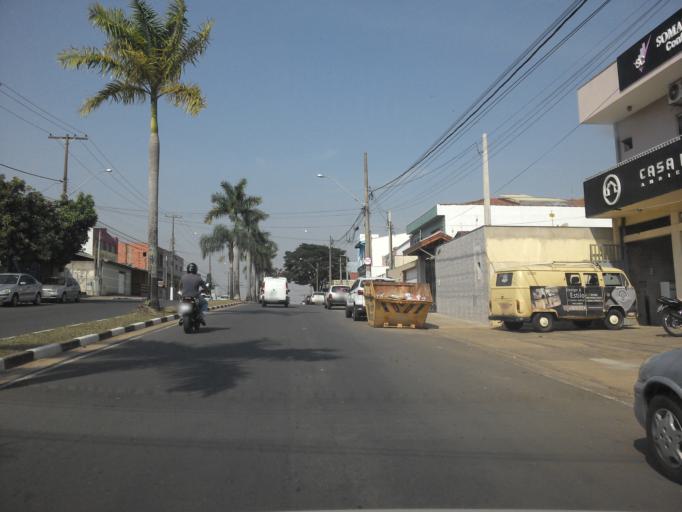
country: BR
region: Sao Paulo
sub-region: Hortolandia
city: Hortolandia
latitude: -22.8565
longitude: -47.2231
